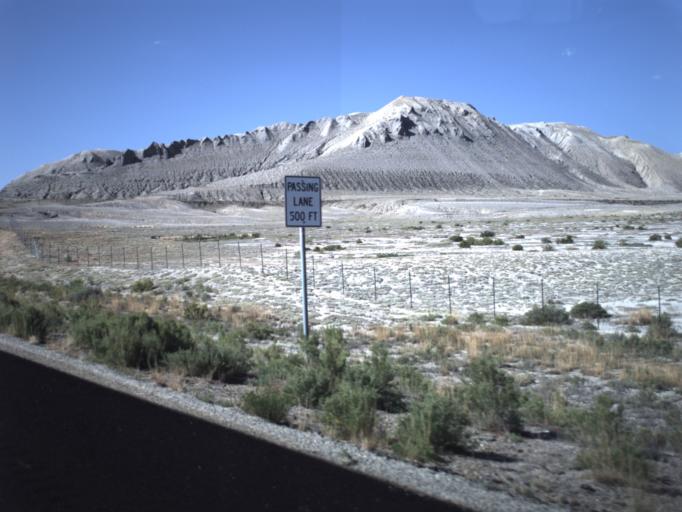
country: US
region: Utah
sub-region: Emery County
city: Ferron
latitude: 39.0491
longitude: -111.1227
